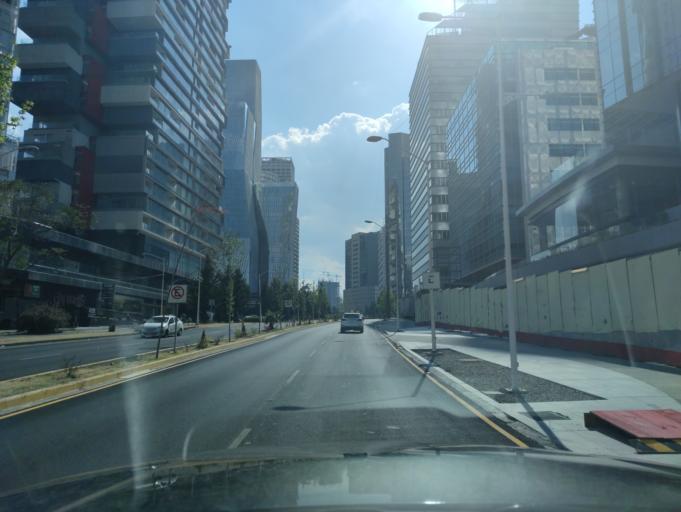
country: MX
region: Mexico City
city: Col. Bosques de las Lomas
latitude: 19.3591
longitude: -99.2714
